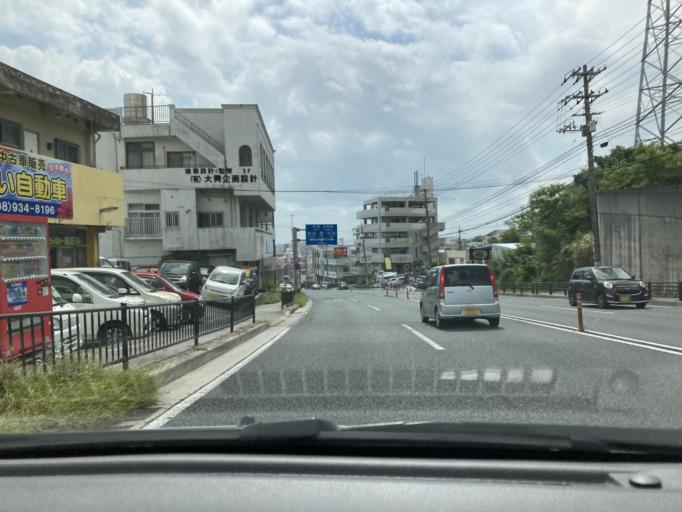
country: JP
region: Okinawa
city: Okinawa
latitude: 26.3289
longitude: 127.8223
